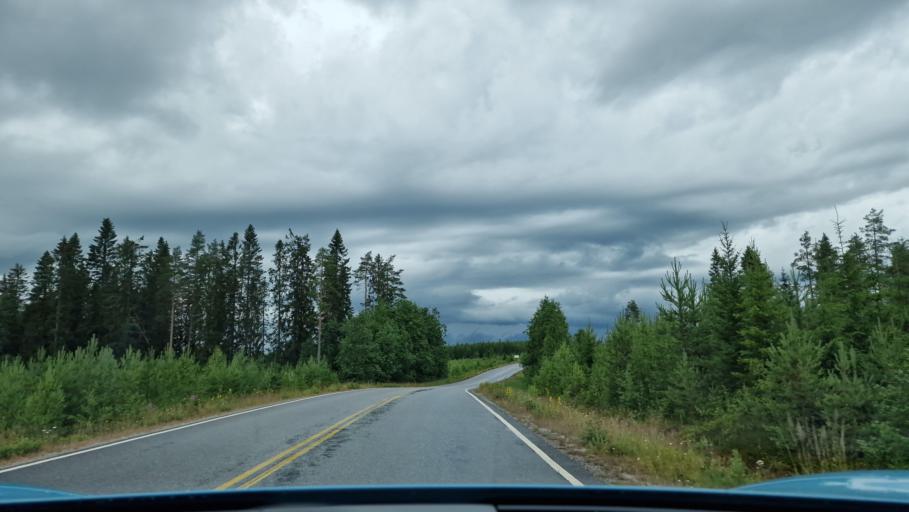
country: FI
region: Southern Ostrobothnia
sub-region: Jaerviseutu
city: Soini
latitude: 62.7096
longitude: 24.4439
